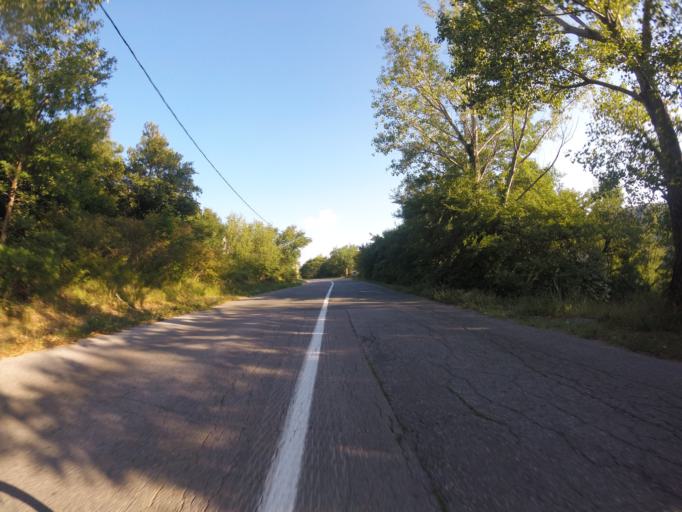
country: HR
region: Primorsko-Goranska
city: Selce
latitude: 45.1772
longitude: 14.7409
